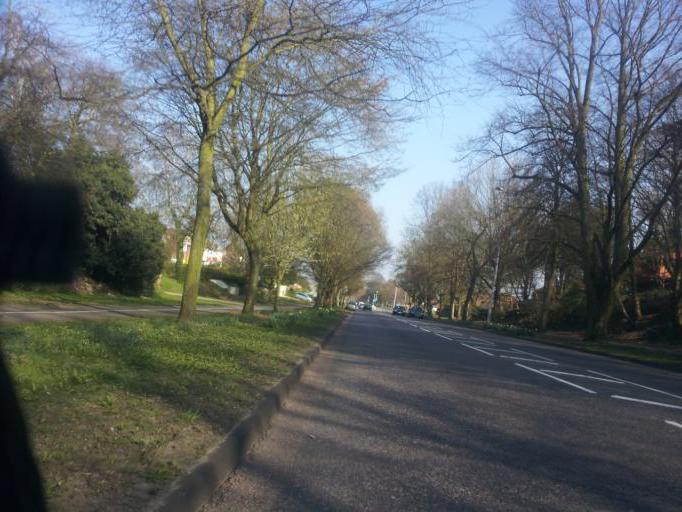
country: GB
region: England
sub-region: Kent
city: Strood
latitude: 51.3983
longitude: 0.4717
